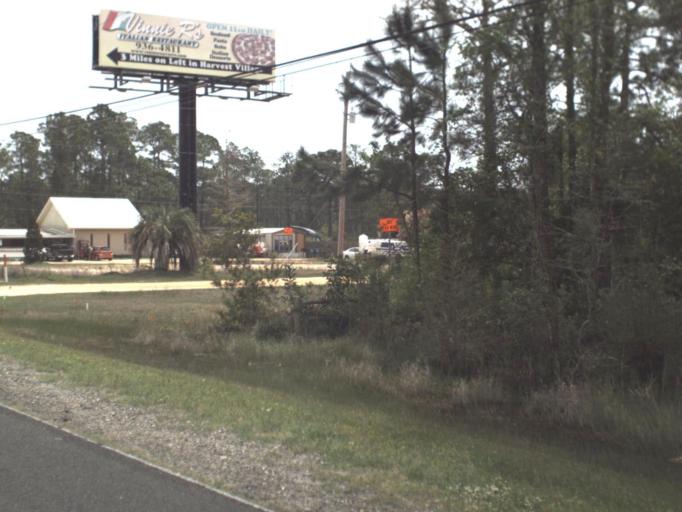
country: US
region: Florida
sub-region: Santa Rosa County
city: Woodlawn Beach
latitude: 30.4038
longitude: -86.9638
